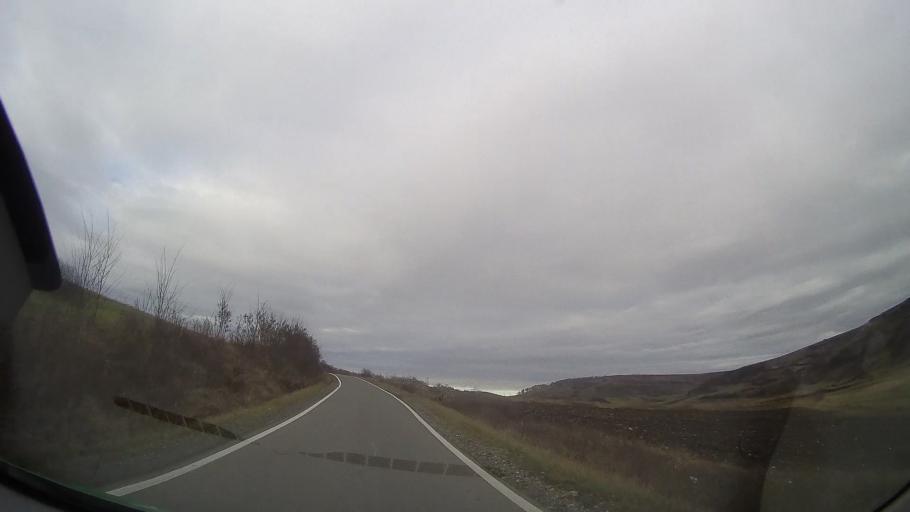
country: RO
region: Mures
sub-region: Comuna Faragau
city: Faragau
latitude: 46.7657
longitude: 24.5584
